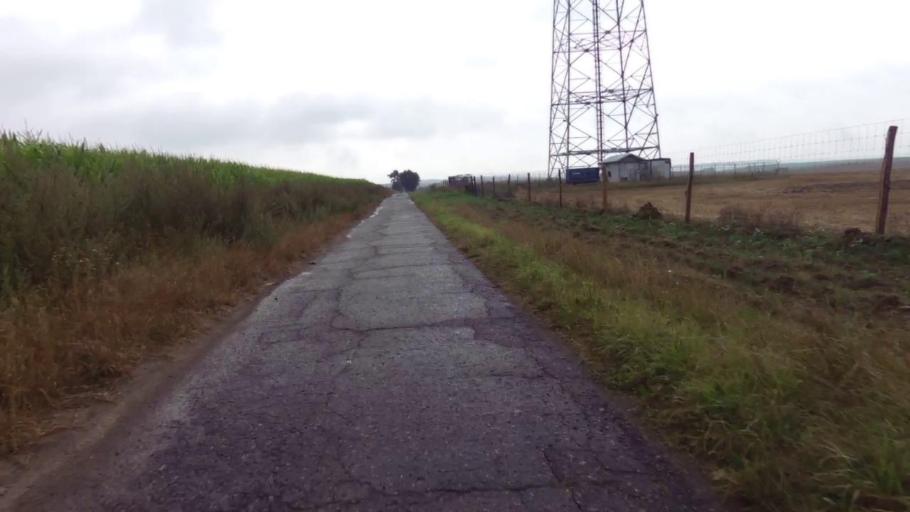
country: PL
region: West Pomeranian Voivodeship
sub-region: Powiat choszczenski
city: Recz
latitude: 53.2654
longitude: 15.4610
